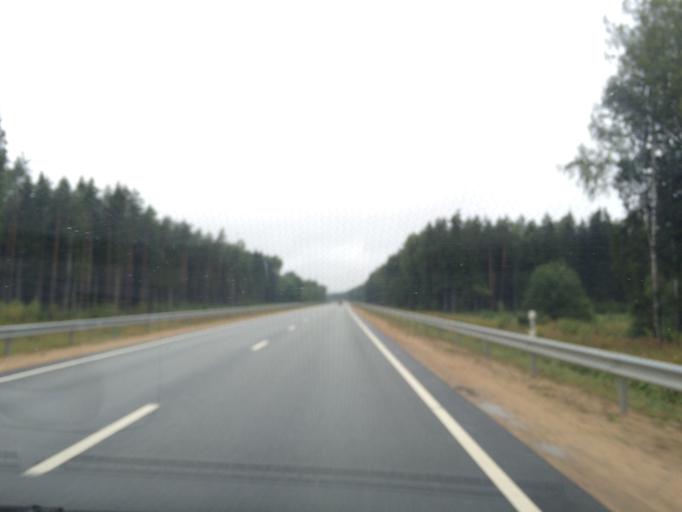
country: LV
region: Kegums
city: Kegums
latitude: 56.8279
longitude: 24.7463
